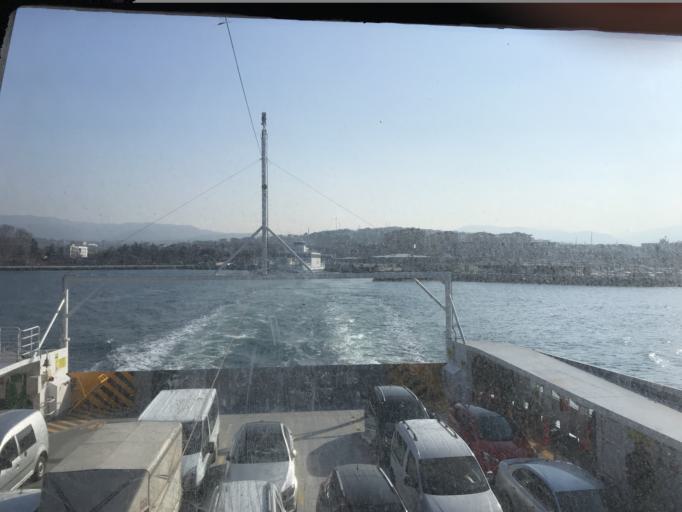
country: TR
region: Yalova
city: Yalova
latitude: 40.6636
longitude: 29.2790
